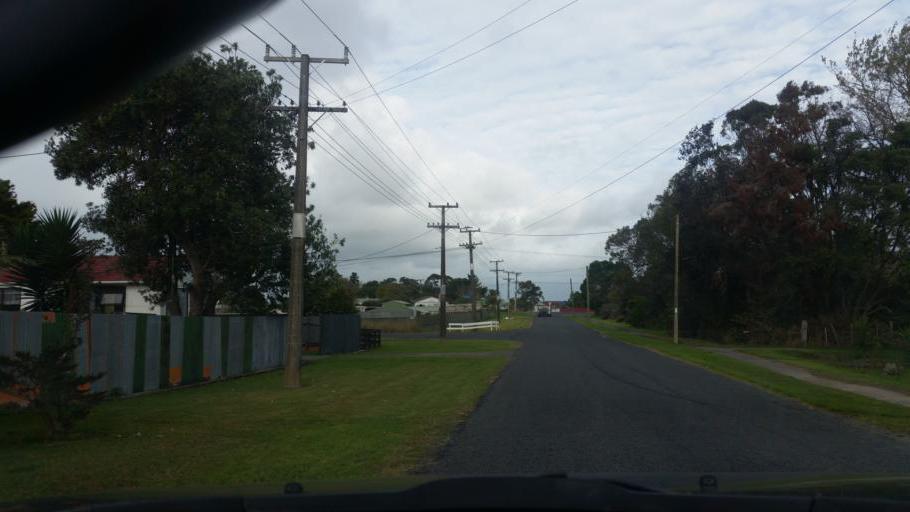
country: NZ
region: Northland
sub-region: Kaipara District
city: Dargaville
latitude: -36.0305
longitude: 173.9171
